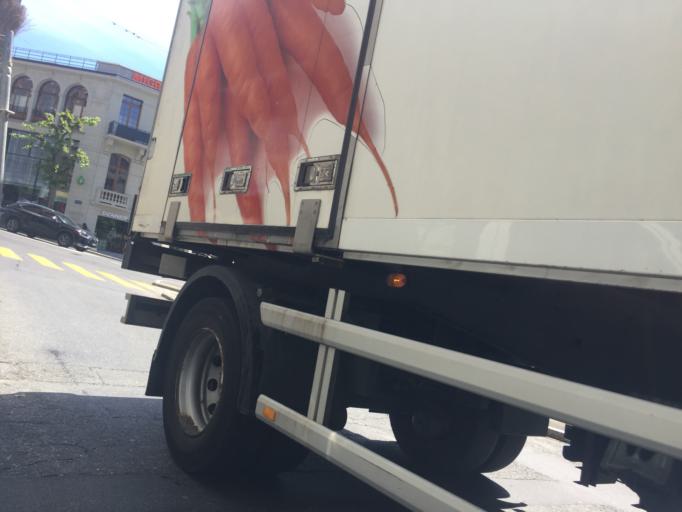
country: CH
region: Vaud
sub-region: Lausanne District
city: Lausanne
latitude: 46.5150
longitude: 6.6320
